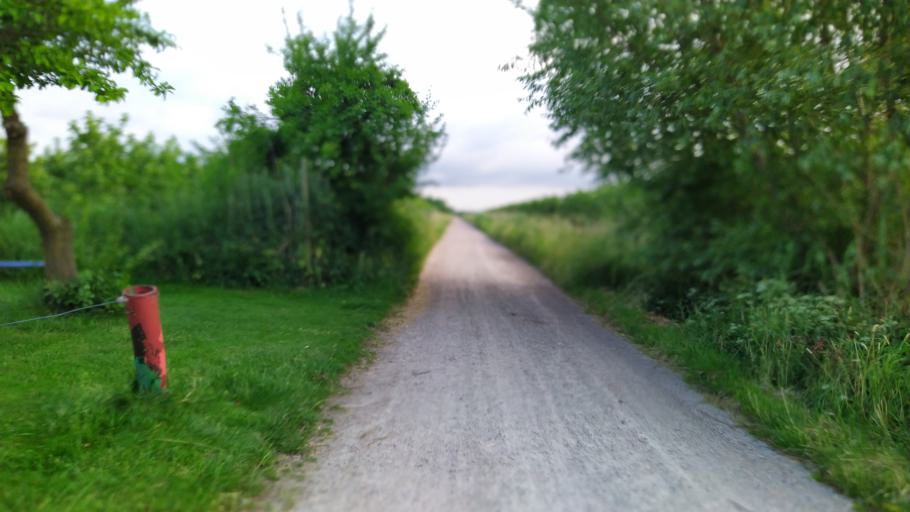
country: DE
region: Lower Saxony
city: Neu Wulmstorf
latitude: 53.5116
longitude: 9.8109
